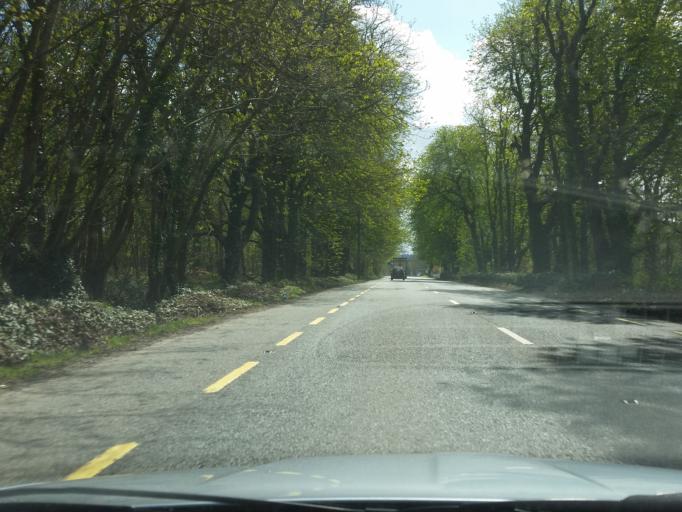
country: IE
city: Kentstown
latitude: 53.6289
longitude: -6.4911
